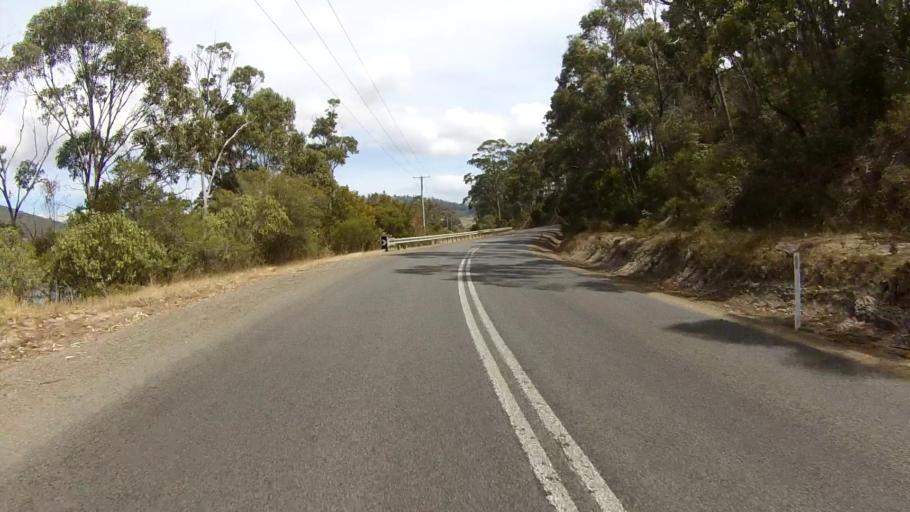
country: AU
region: Tasmania
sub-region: Huon Valley
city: Cygnet
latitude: -43.1828
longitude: 147.0966
